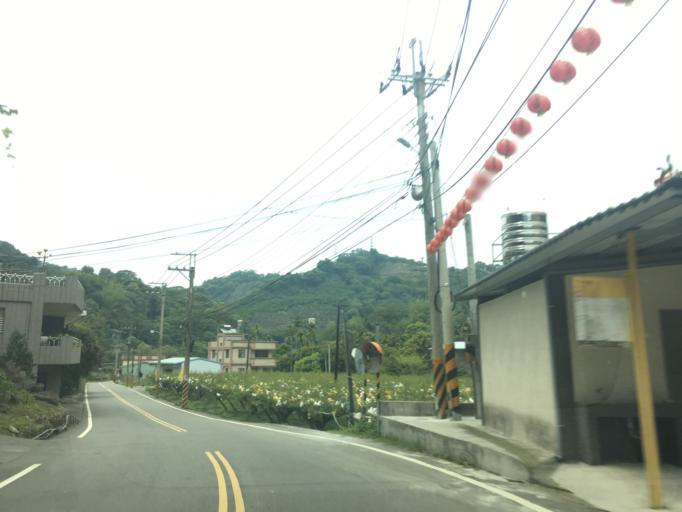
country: TW
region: Taiwan
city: Fengyuan
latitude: 24.1628
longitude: 120.8261
